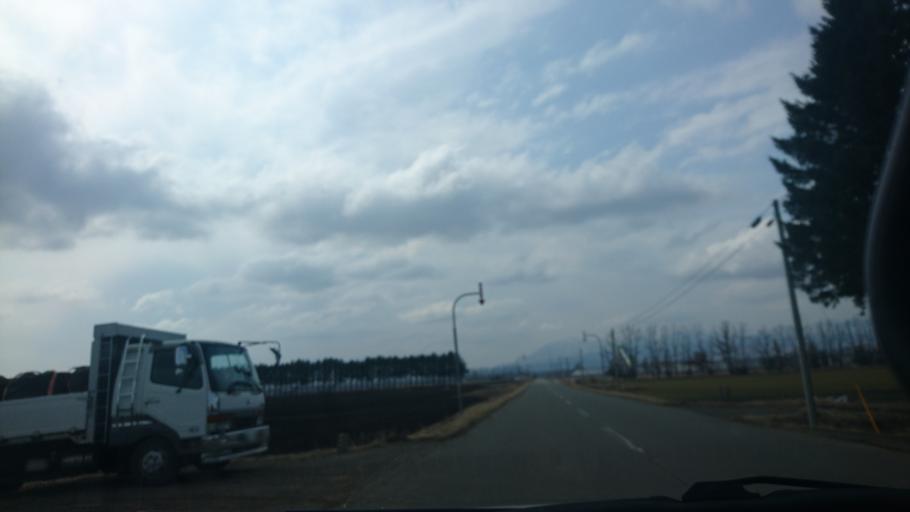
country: JP
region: Hokkaido
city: Otofuke
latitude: 43.2156
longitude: 143.2868
